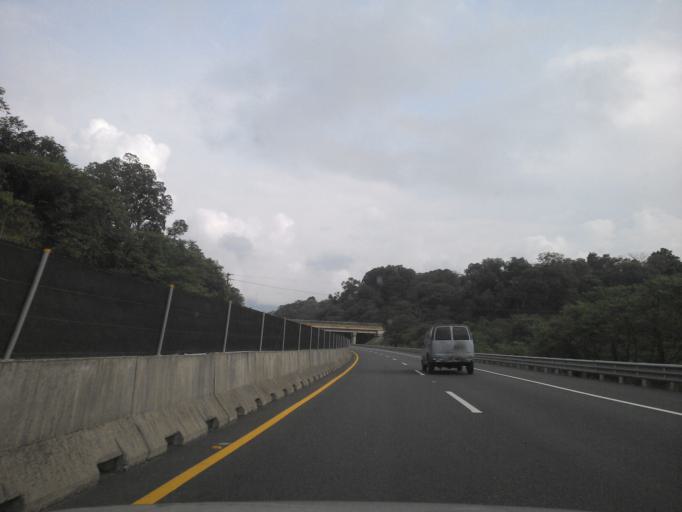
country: MX
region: Puebla
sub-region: Xicotepec
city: San Lorenzo
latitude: 20.3889
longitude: -97.9462
